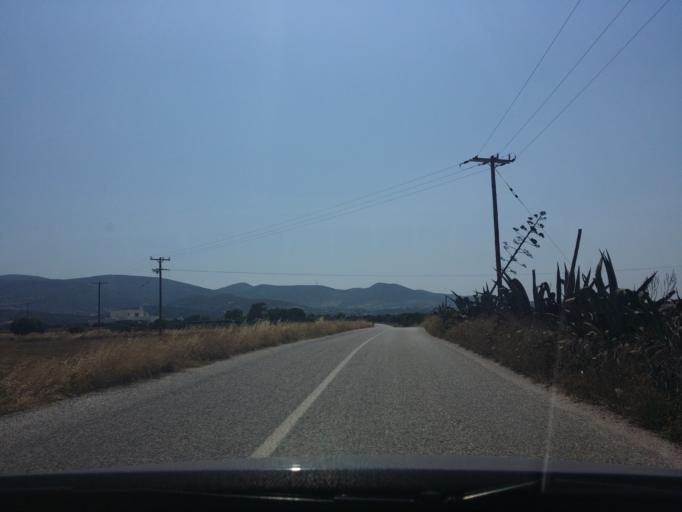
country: GR
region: South Aegean
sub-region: Nomos Kykladon
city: Antiparos
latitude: 37.0088
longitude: 25.1164
